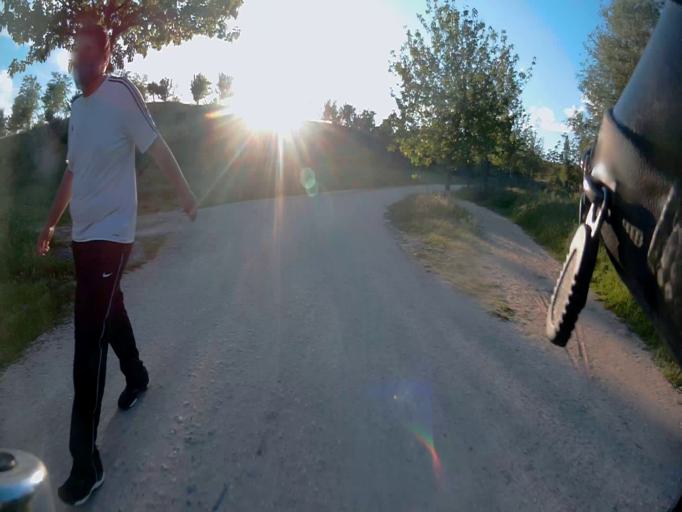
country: ES
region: Madrid
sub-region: Provincia de Madrid
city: Fuenlabrada
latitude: 40.3163
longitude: -3.7948
